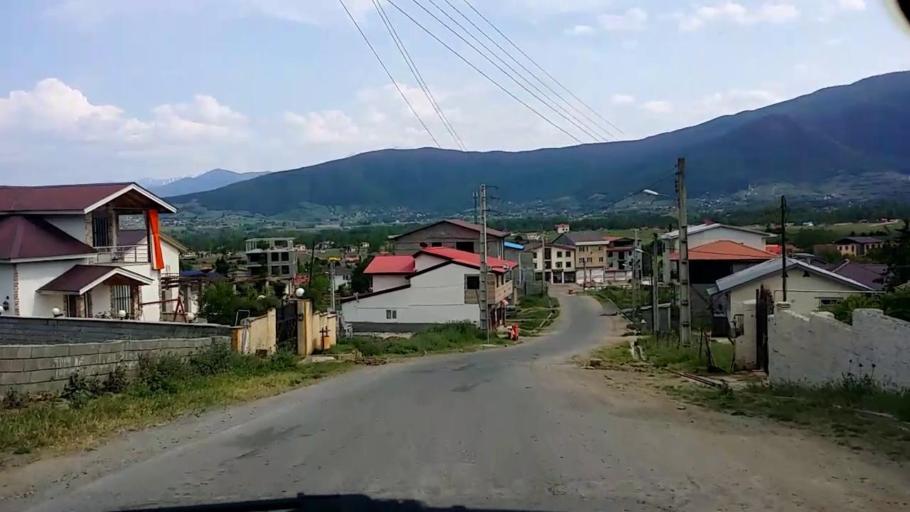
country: IR
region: Mazandaran
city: `Abbasabad
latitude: 36.5488
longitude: 51.1850
